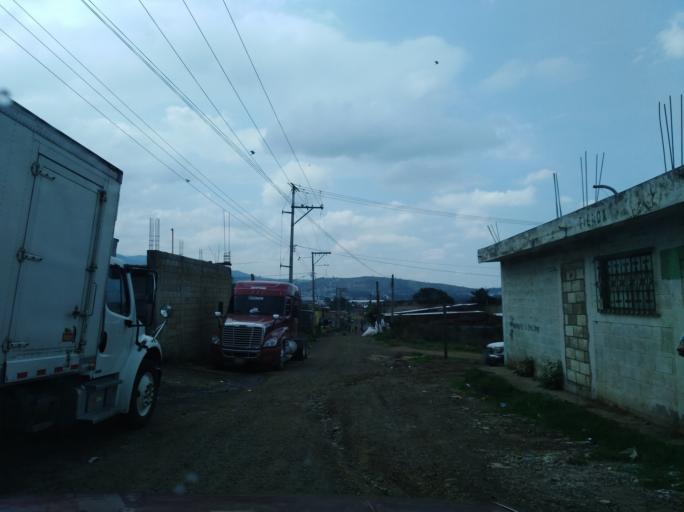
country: GT
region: Guatemala
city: Villa Nueva
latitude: 14.5241
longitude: -90.6203
